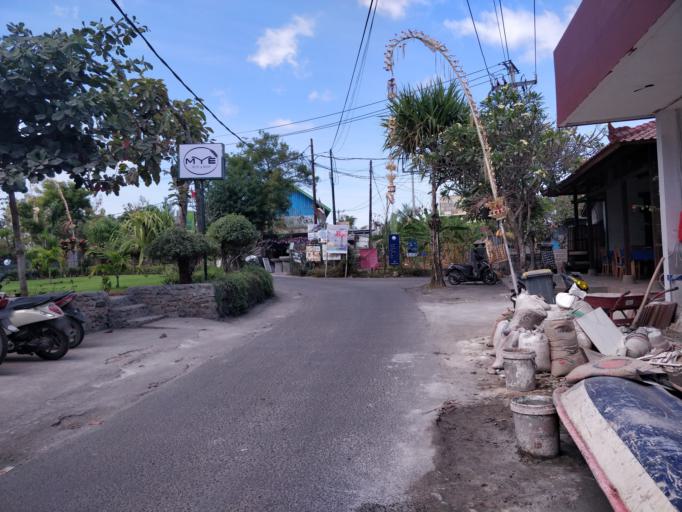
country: ID
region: Bali
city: Lembongan Kawan
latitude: -8.6878
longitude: 115.4372
